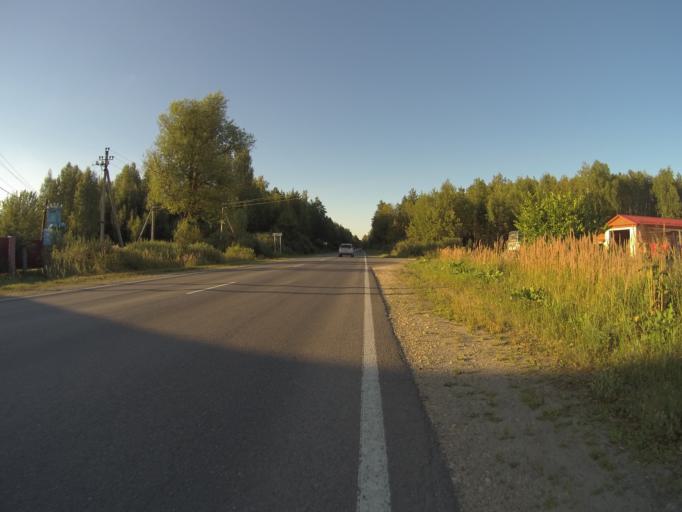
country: RU
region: Vladimir
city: Anopino
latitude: 55.6902
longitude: 40.7467
